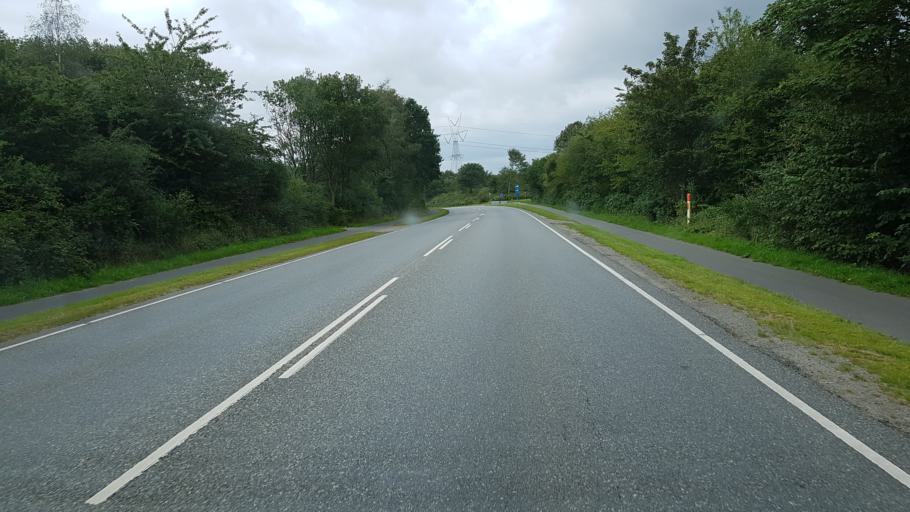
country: DK
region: South Denmark
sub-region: Kolding Kommune
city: Kolding
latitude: 55.4825
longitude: 9.4325
